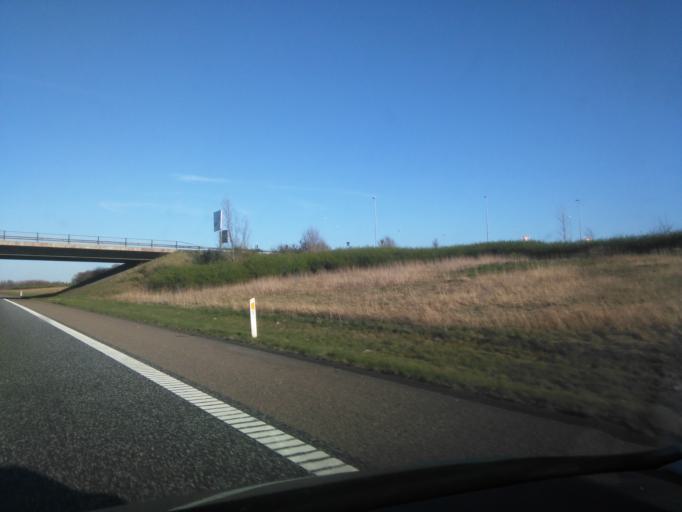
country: DK
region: Central Jutland
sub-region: Herning Kommune
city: Hammerum
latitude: 56.1203
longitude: 9.0475
